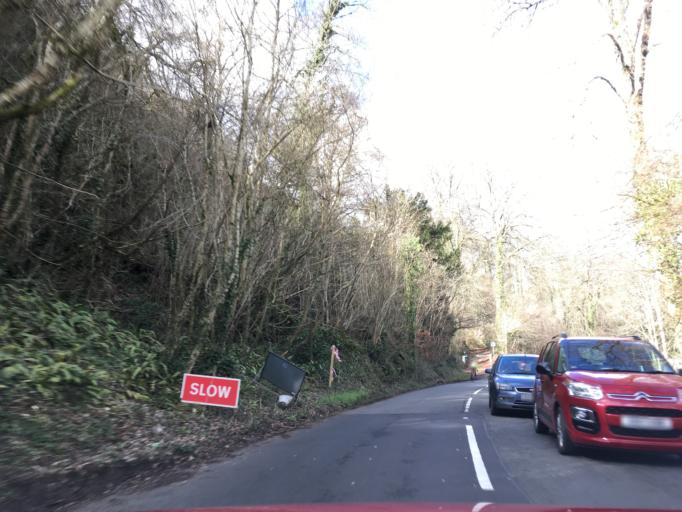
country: GB
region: Wales
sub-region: Monmouthshire
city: Tintern
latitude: 51.6795
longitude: -2.6760
